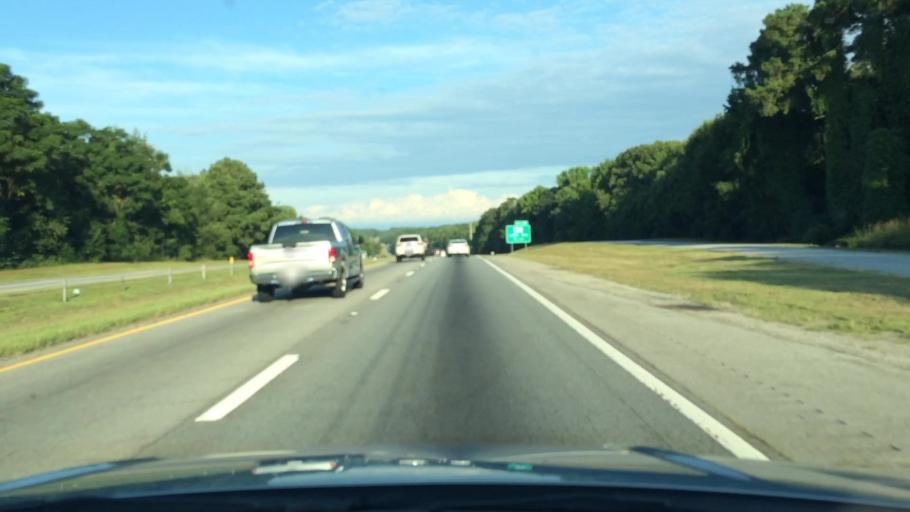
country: US
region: South Carolina
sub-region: Lexington County
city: Chapin
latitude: 34.2268
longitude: -81.4296
